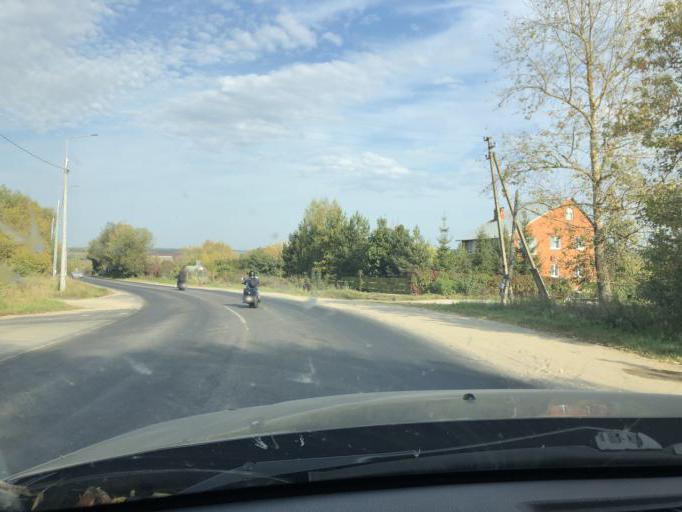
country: RU
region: Tula
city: Leninskiy
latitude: 54.2955
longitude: 37.4566
